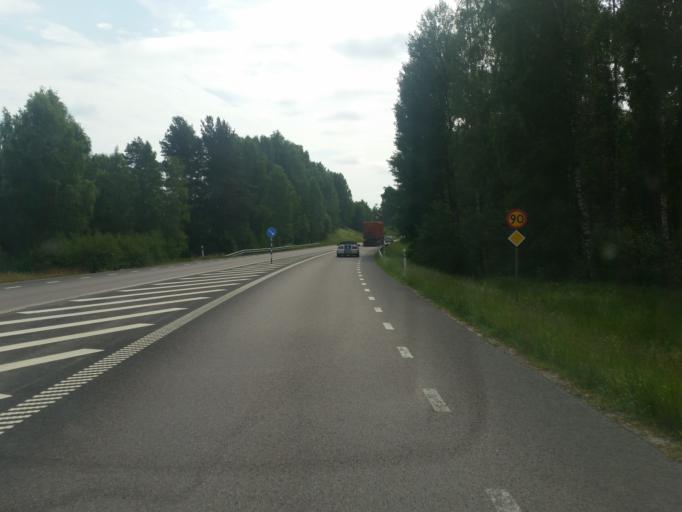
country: SE
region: Dalarna
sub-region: Gagnefs Kommun
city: Gagnef
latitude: 60.6003
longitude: 15.0681
